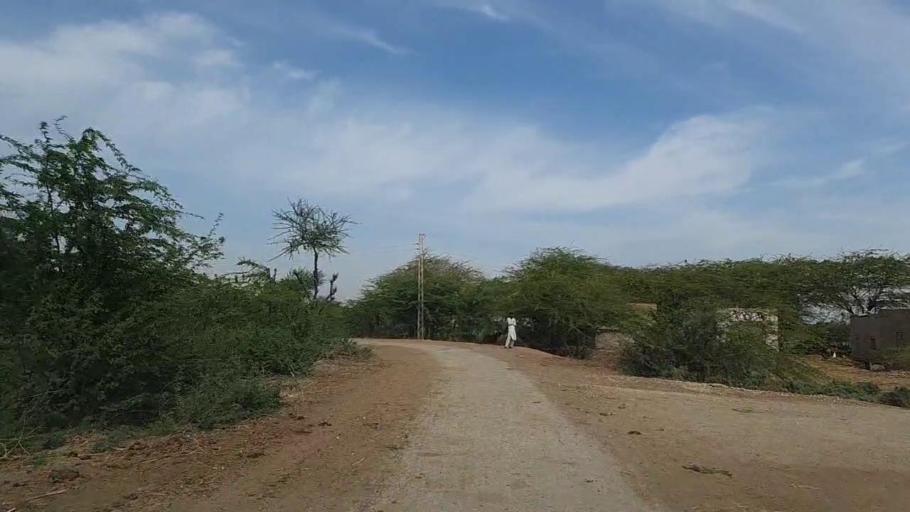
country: PK
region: Sindh
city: Samaro
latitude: 25.2999
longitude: 69.4239
